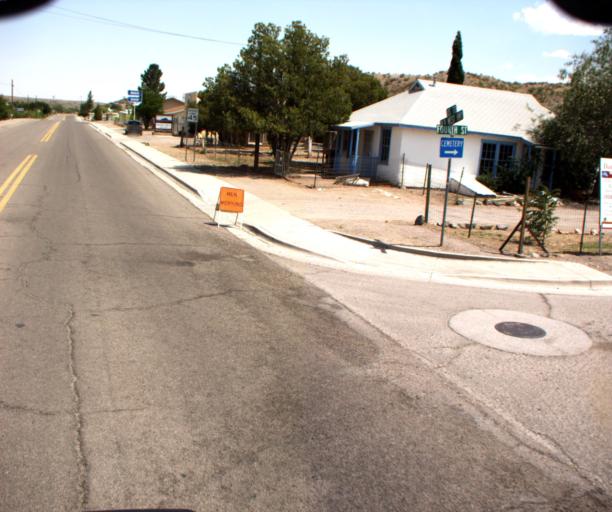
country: US
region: Arizona
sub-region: Greenlee County
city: Clifton
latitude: 32.7135
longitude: -109.0990
